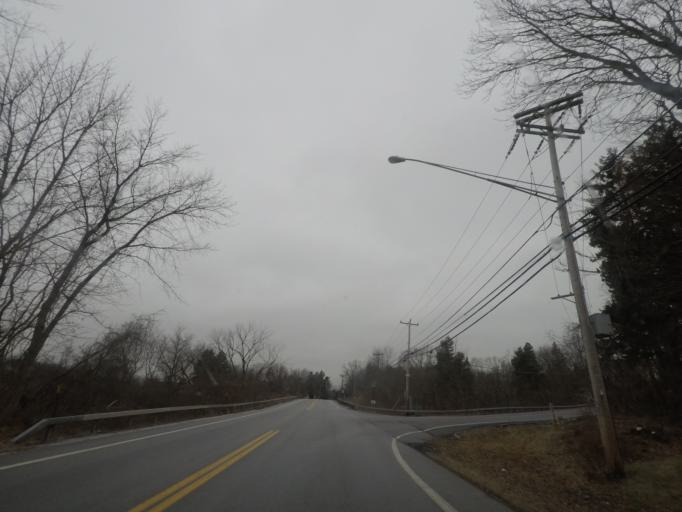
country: US
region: New York
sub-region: Saratoga County
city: Mechanicville
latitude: 42.8996
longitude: -73.7082
